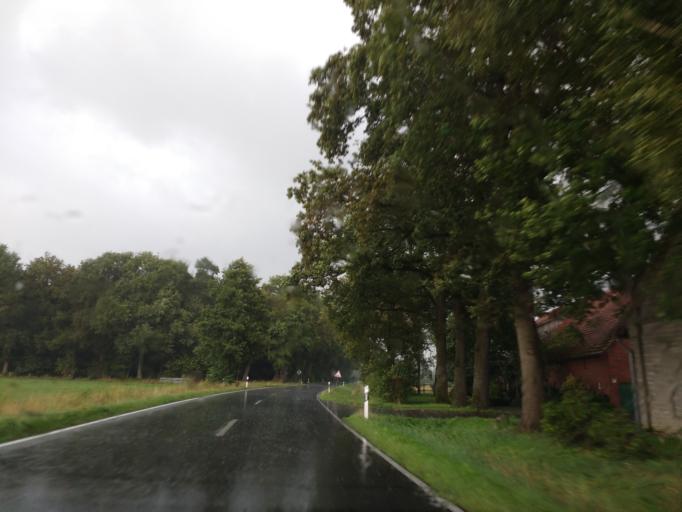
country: DE
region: North Rhine-Westphalia
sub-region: Regierungsbezirk Munster
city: Lienen
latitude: 52.1144
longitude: 7.9247
